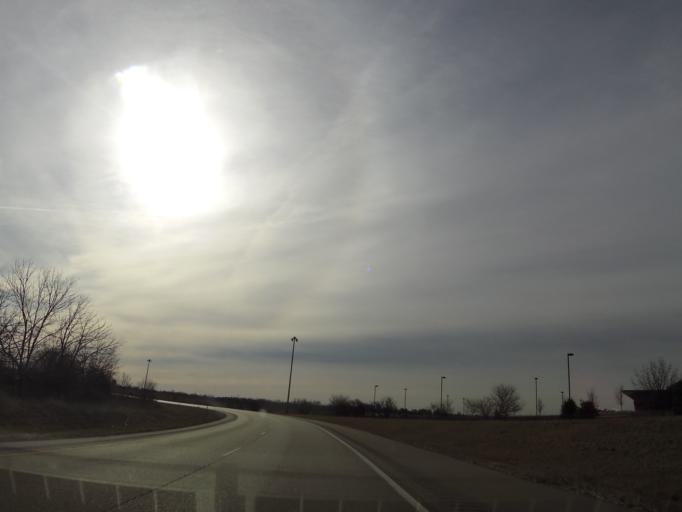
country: US
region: Illinois
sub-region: McLean County
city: Normal
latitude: 40.5372
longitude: -89.0123
